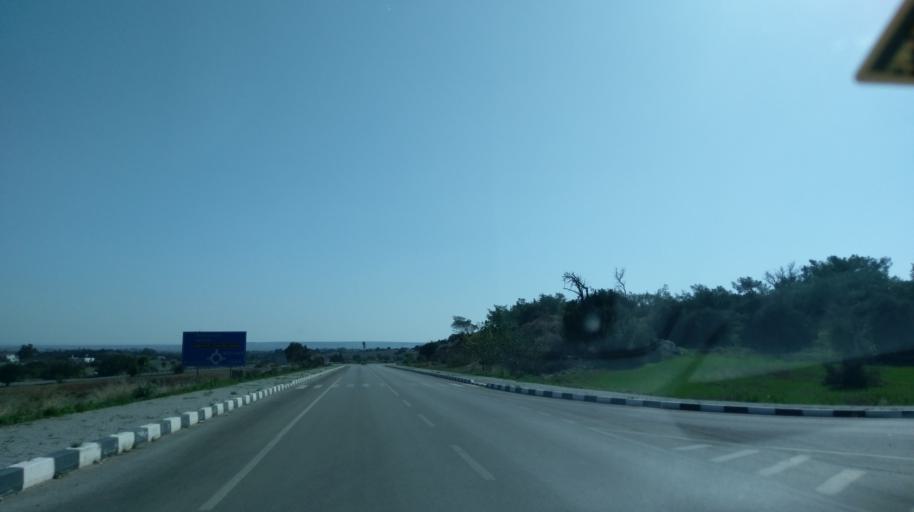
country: CY
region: Ammochostos
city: Trikomo
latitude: 35.4072
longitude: 33.9904
